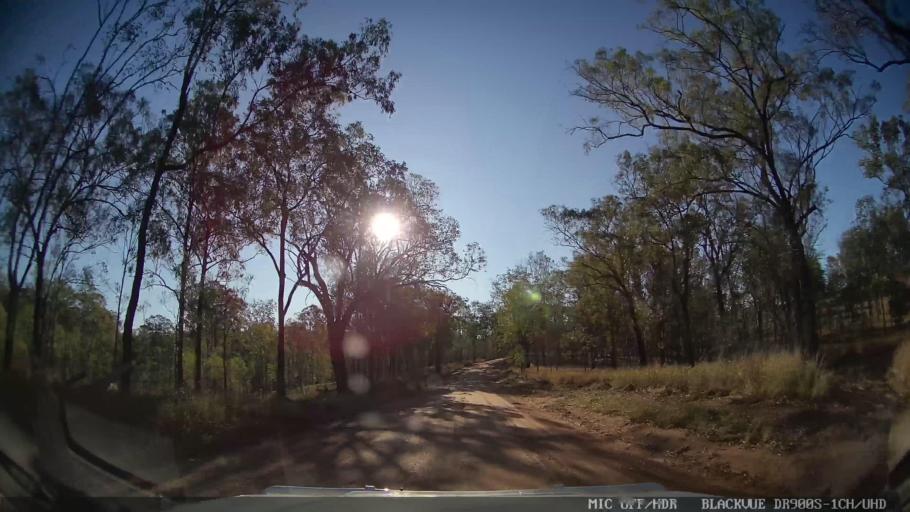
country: AU
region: Queensland
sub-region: Bundaberg
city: Sharon
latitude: -24.7395
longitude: 151.5250
